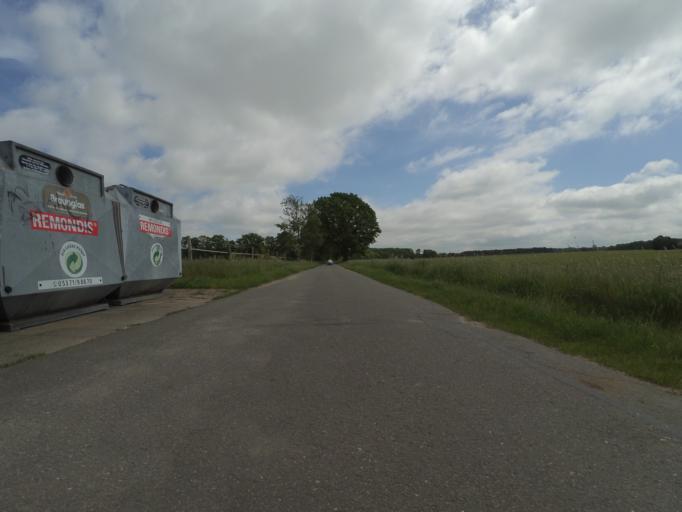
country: DE
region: Lower Saxony
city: Ribbesbuttel
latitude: 52.4306
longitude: 10.4875
